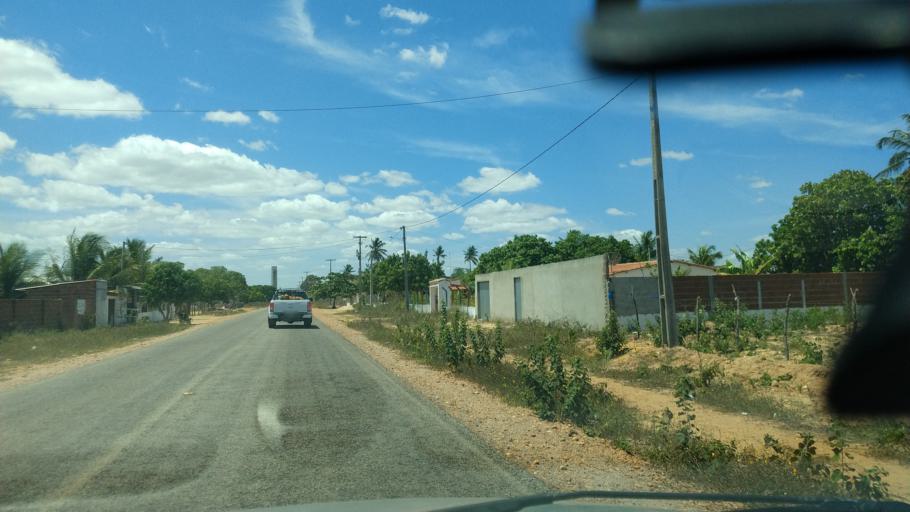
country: BR
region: Rio Grande do Norte
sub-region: Sao Paulo Do Potengi
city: Sao Paulo do Potengi
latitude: -5.9162
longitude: -35.7239
